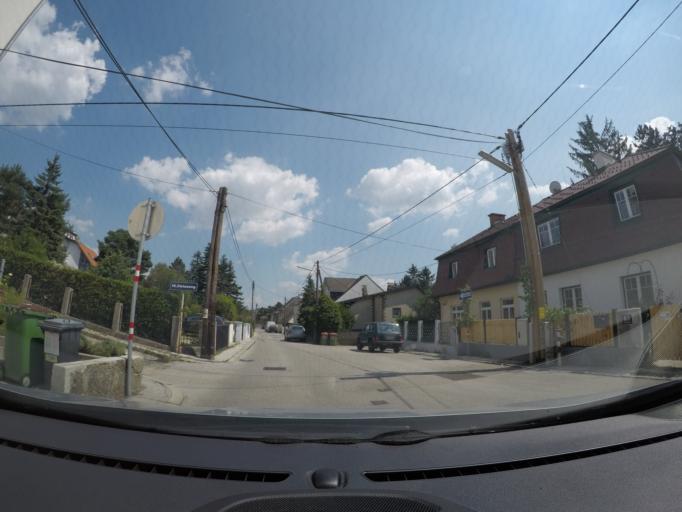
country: AT
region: Lower Austria
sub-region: Politischer Bezirk Wien-Umgebung
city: Purkersdorf
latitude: 48.2065
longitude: 16.2474
